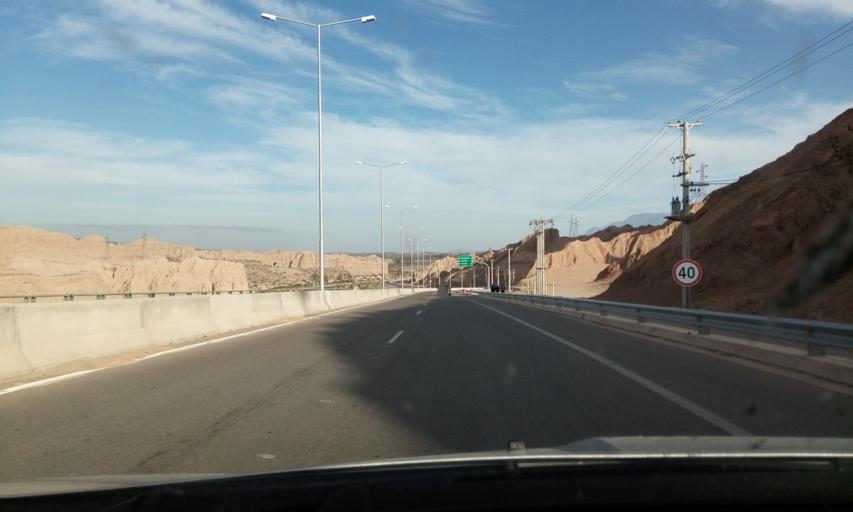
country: AR
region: San Juan
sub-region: Departamento de Rivadavia
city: Rivadavia
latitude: -31.4765
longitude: -68.6512
